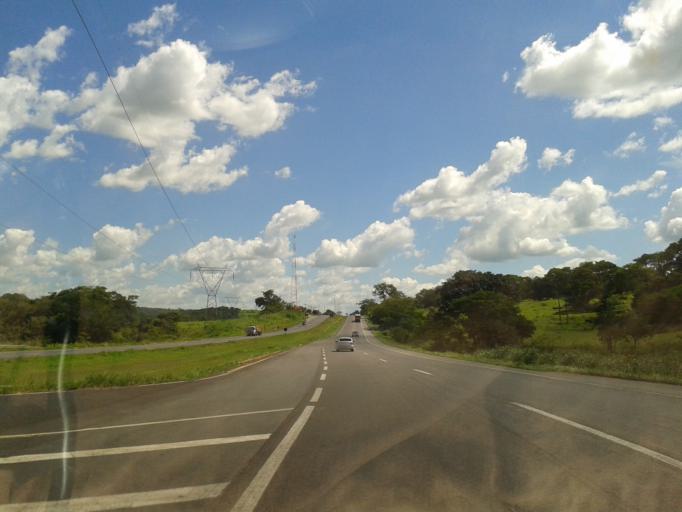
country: BR
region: Goias
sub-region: Piracanjuba
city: Piracanjuba
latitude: -17.4057
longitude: -49.2244
